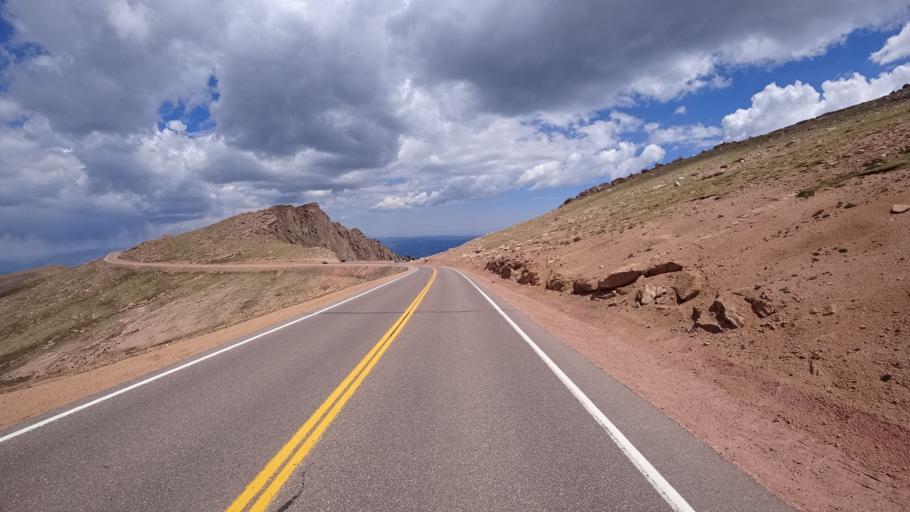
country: US
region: Colorado
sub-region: El Paso County
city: Cascade-Chipita Park
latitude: 38.8546
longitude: -105.0632
